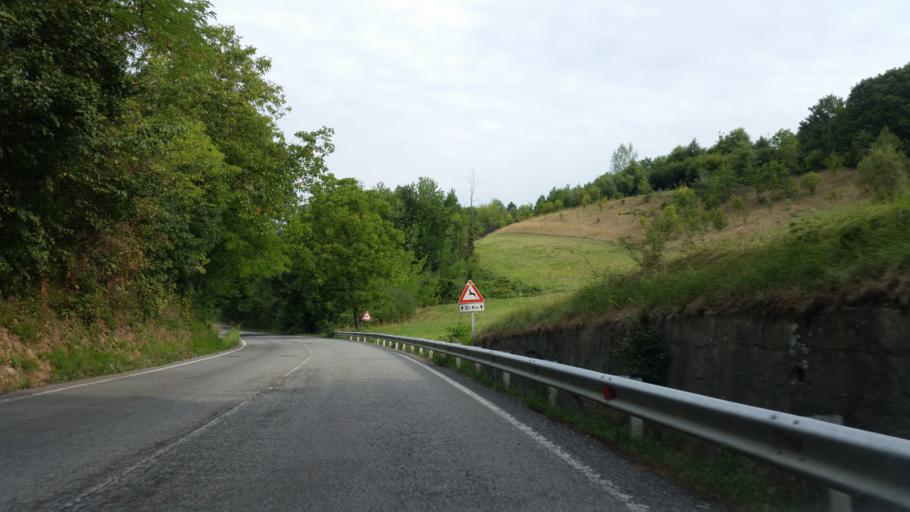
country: IT
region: Piedmont
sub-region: Provincia di Torino
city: Brozolo
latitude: 45.1154
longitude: 8.0665
